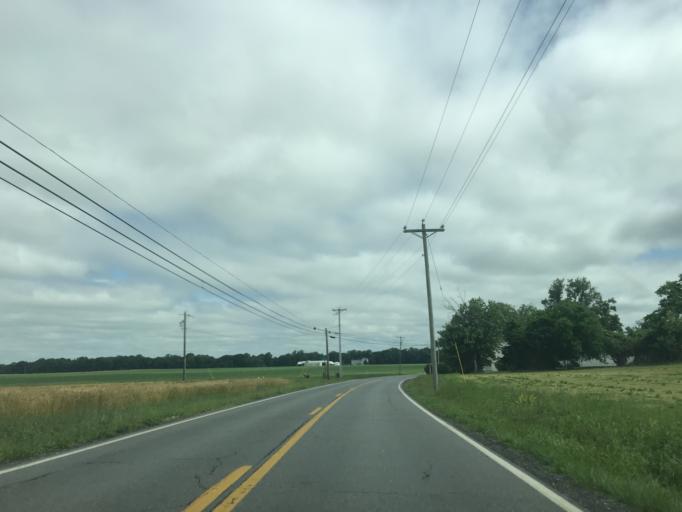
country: US
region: Maryland
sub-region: Caroline County
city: Ridgely
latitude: 38.9056
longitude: -75.9585
